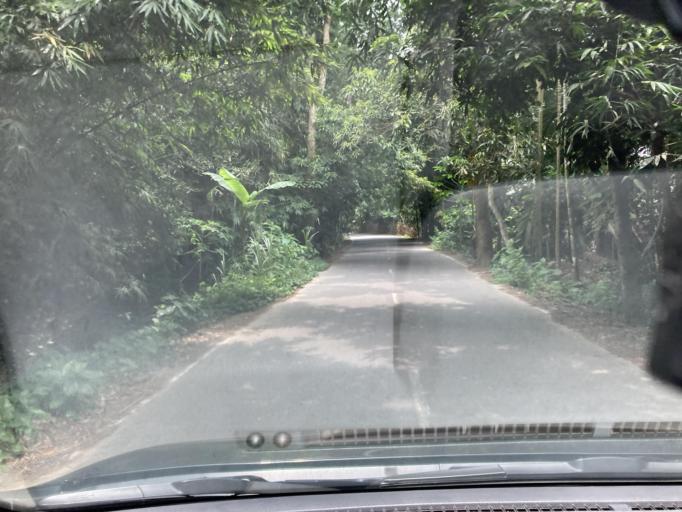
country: BD
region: Dhaka
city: Dohar
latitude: 23.7911
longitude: 90.0597
